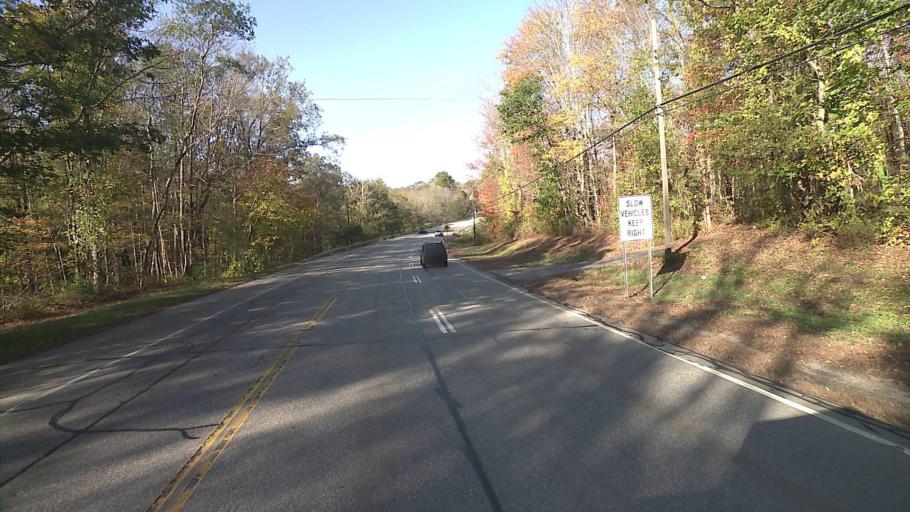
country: US
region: Connecticut
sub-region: Windham County
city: Windham
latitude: 41.7669
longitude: -72.0538
